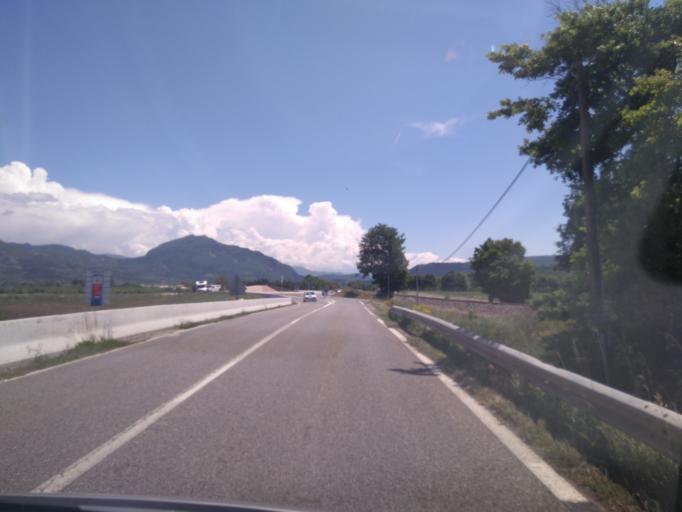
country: FR
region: Provence-Alpes-Cote d'Azur
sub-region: Departement des Alpes-de-Haute-Provence
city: Sisteron
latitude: 44.2335
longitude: 5.9037
